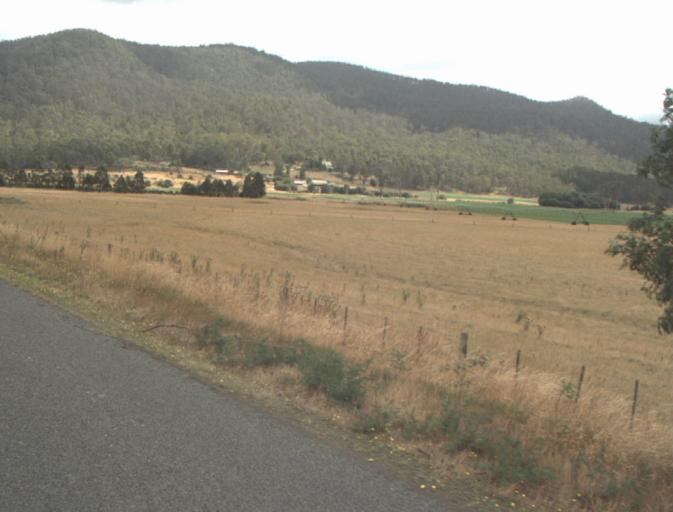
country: AU
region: Tasmania
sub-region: Northern Midlands
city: Evandale
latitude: -41.4959
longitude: 147.4479
